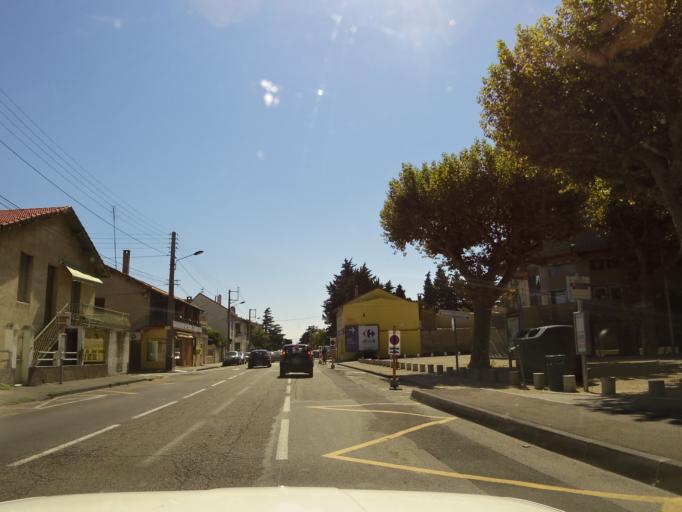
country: FR
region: Languedoc-Roussillon
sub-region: Departement du Gard
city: Nimes
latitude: 43.8281
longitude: 4.3735
